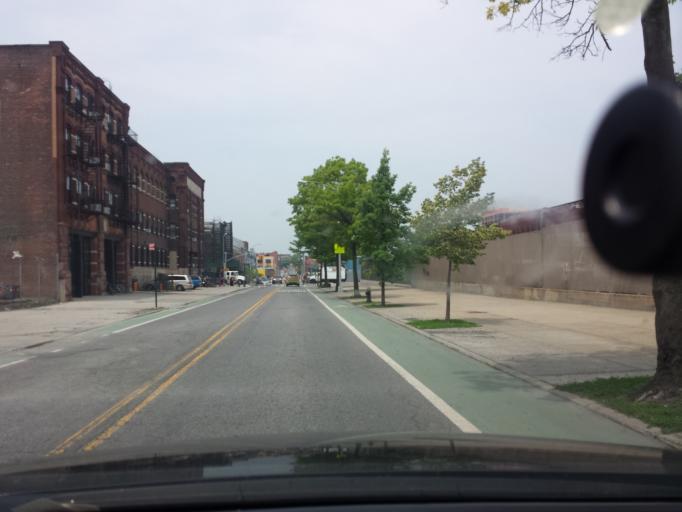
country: US
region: New York
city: New York City
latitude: 40.6745
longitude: -73.9869
